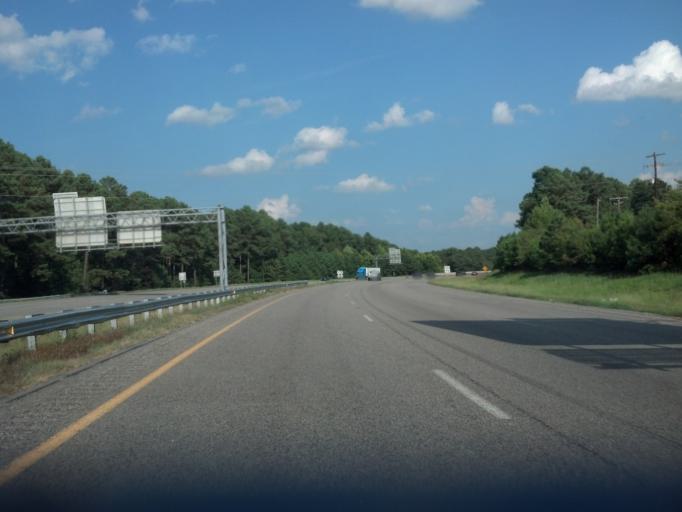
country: US
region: North Carolina
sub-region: Edgecombe County
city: Princeville
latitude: 35.8879
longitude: -77.5437
